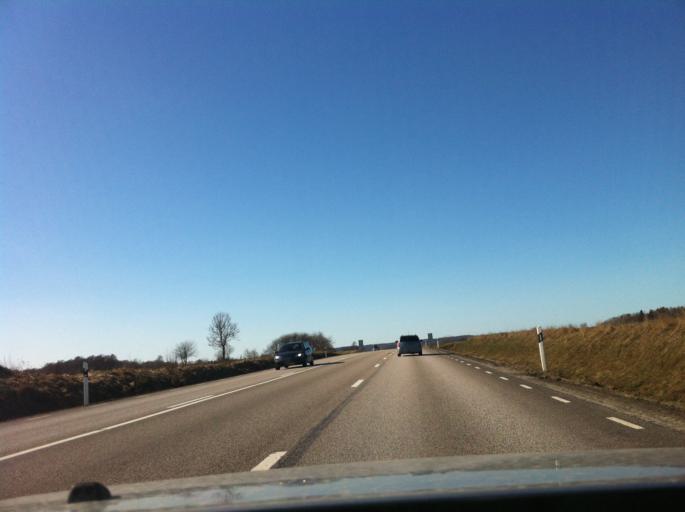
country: SE
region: Vaestra Goetaland
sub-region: Falkopings Kommun
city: Falkoeping
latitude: 58.1445
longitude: 13.6236
